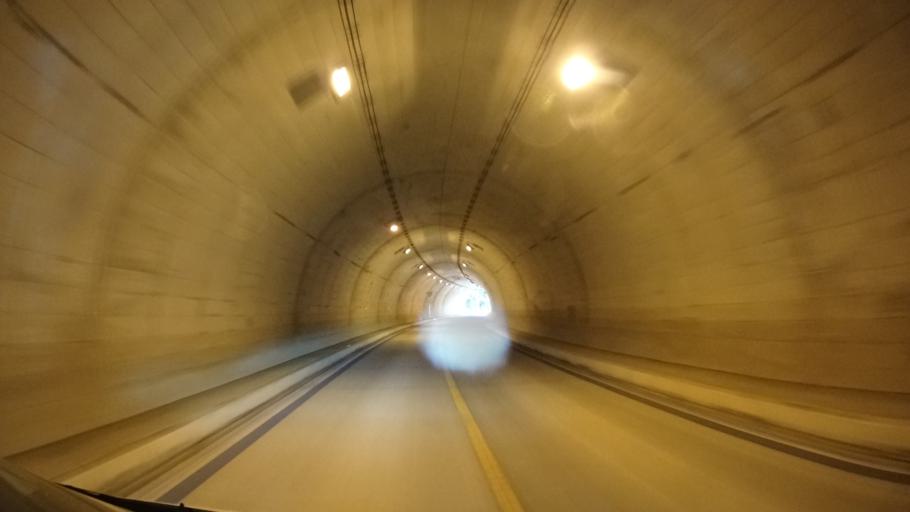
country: JP
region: Kyoto
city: Maizuru
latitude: 35.4336
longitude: 135.4007
